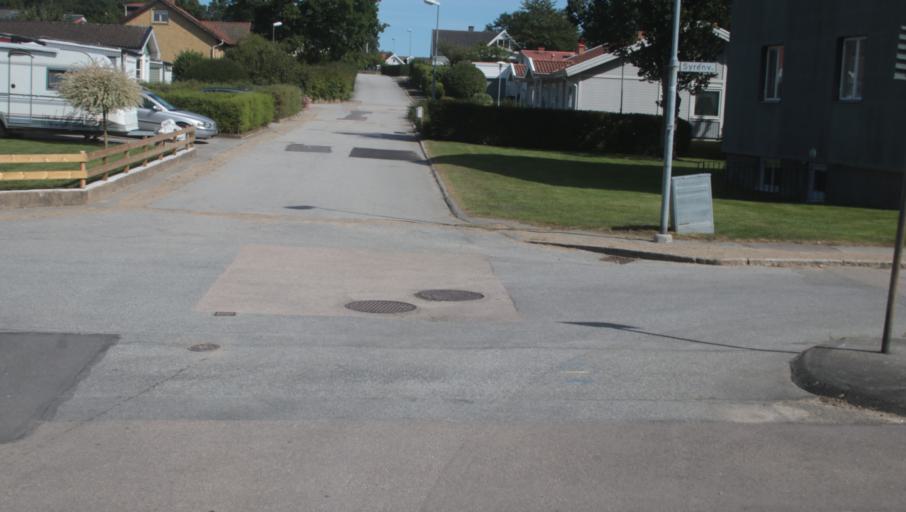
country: SE
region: Blekinge
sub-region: Karlshamns Kommun
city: Karlshamn
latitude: 56.2103
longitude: 14.8385
